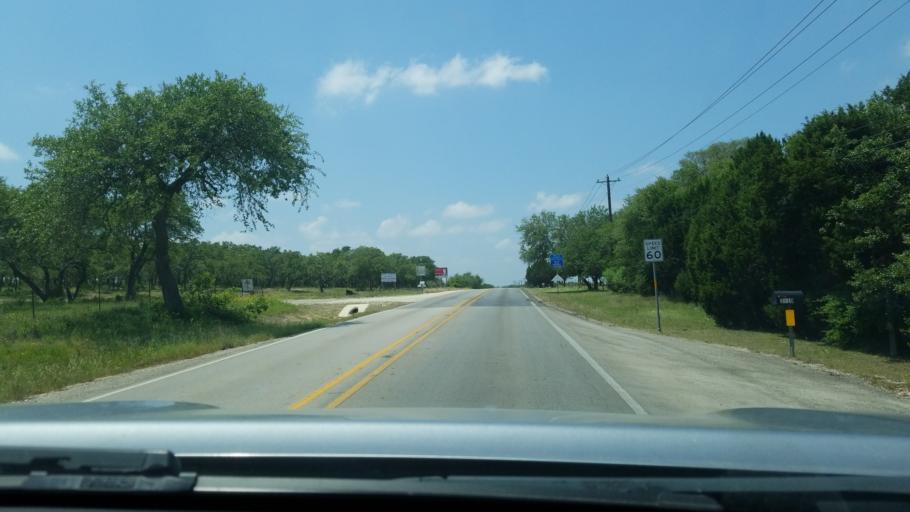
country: US
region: Texas
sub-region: Hays County
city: Woodcreek
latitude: 30.0214
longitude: -98.1548
